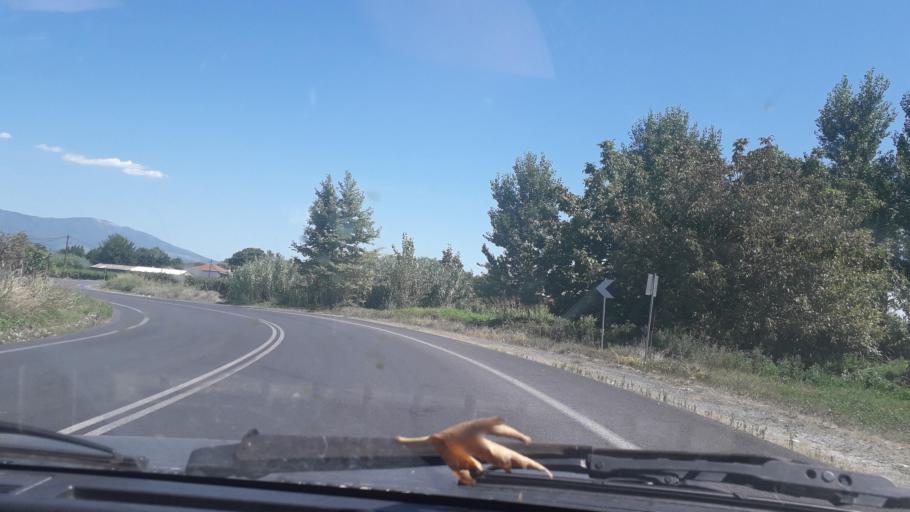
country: GR
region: Central Macedonia
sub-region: Nomos Pellis
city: Tsakoi
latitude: 40.9722
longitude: 22.0113
